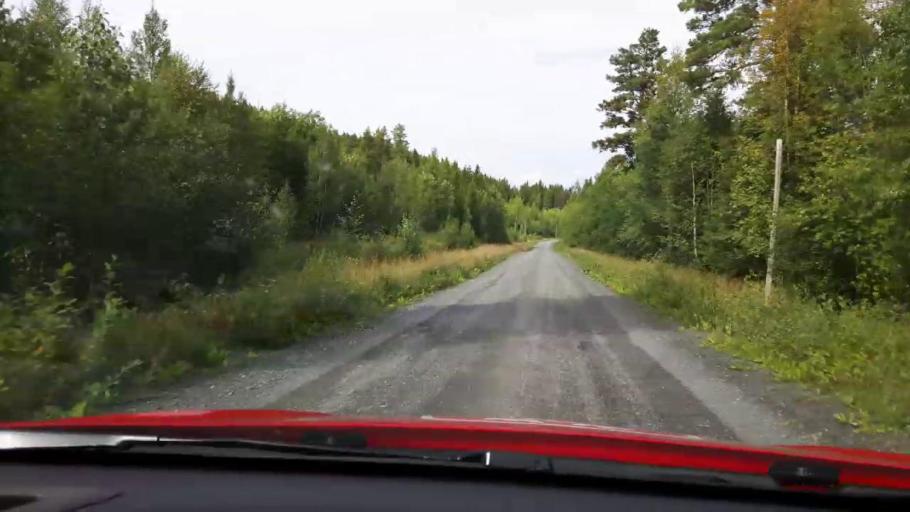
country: SE
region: Jaemtland
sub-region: Are Kommun
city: Jarpen
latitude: 63.2748
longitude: 13.7405
